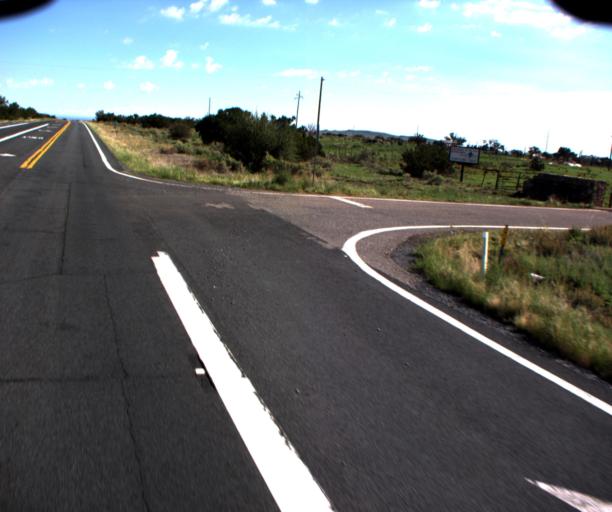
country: US
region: Arizona
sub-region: Coconino County
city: Williams
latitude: 35.5025
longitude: -112.1738
